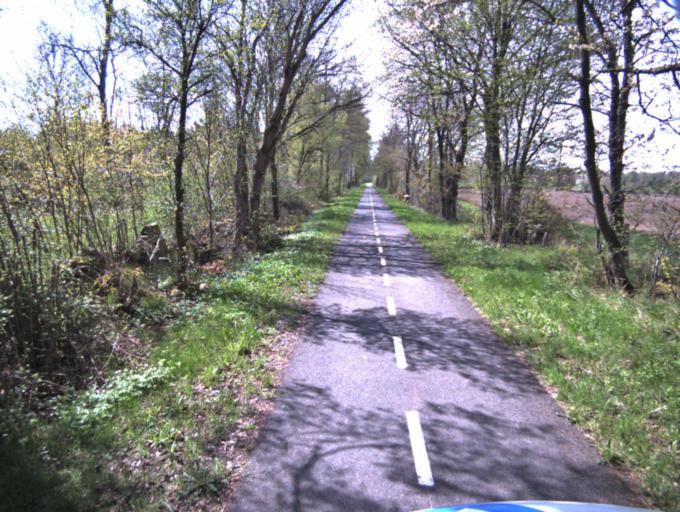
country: SE
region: Skane
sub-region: Kristianstads Kommun
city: Onnestad
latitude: 56.0028
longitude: 14.0467
